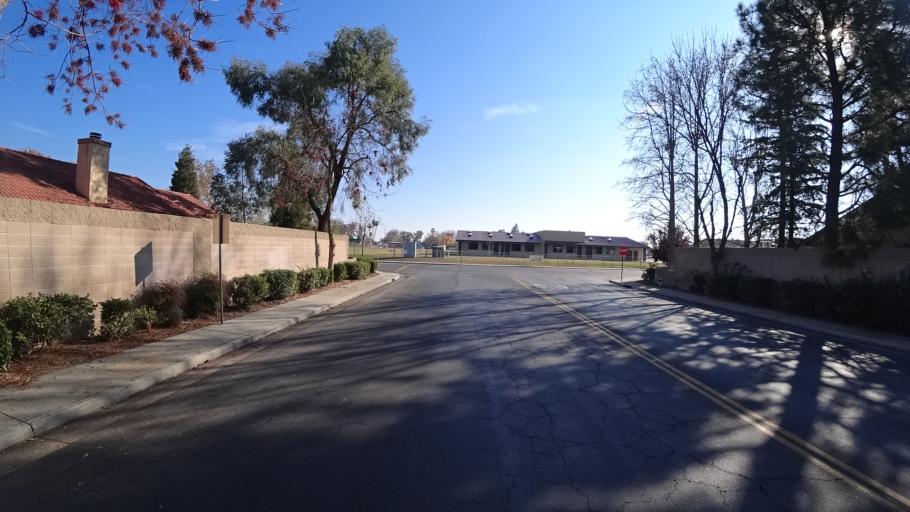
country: US
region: California
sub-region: Kern County
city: Greenacres
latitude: 35.3150
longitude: -119.1031
